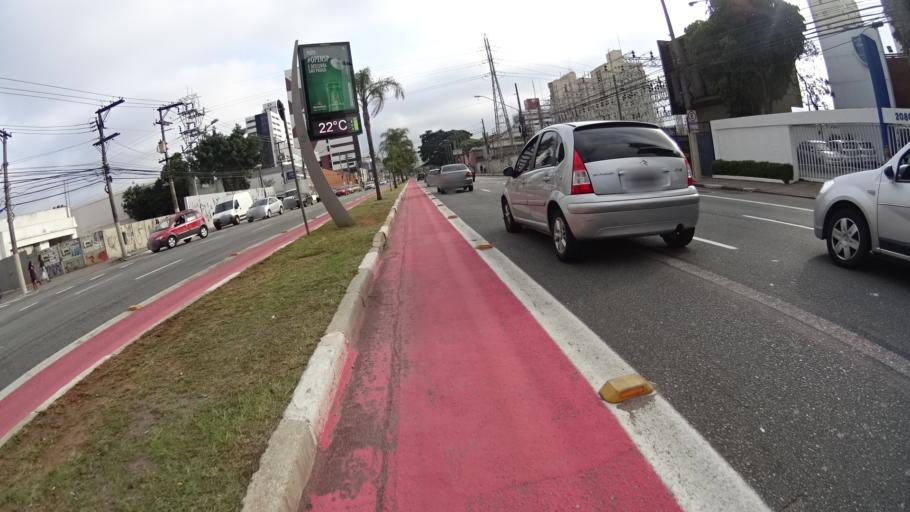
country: BR
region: Sao Paulo
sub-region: Diadema
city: Diadema
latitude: -23.6224
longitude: -46.6401
